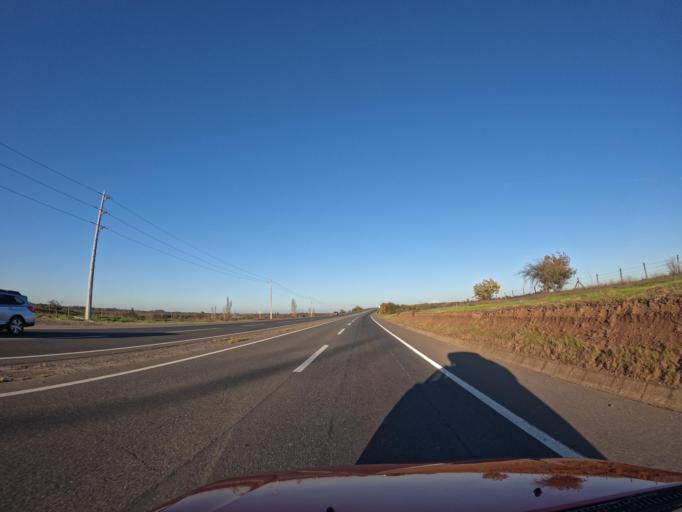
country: CL
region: Biobio
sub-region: Provincia de Nuble
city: Bulnes
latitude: -36.6588
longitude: -72.2759
